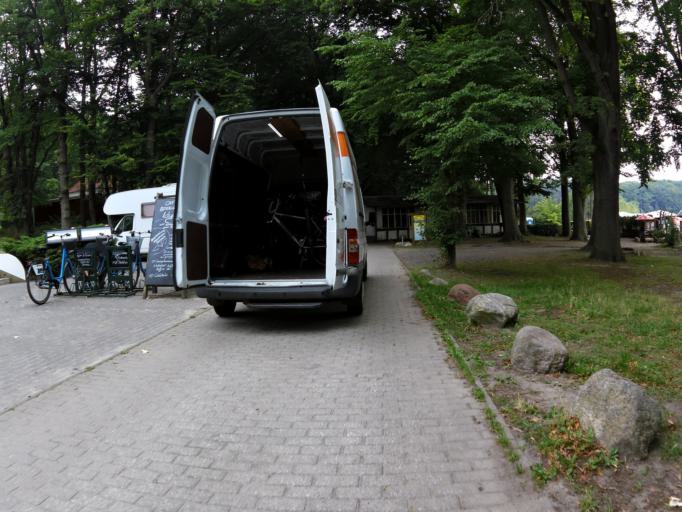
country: DE
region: Mecklenburg-Vorpommern
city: Seebad Heringsdorf
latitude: 53.9181
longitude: 14.1649
